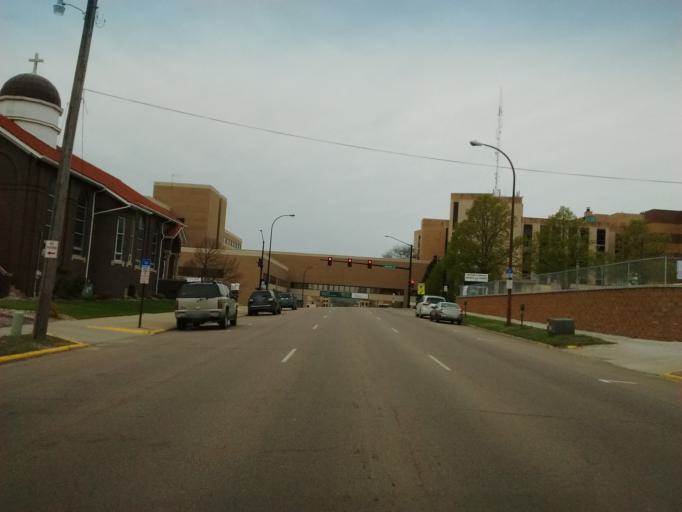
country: US
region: Iowa
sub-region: Woodbury County
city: Sioux City
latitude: 42.4964
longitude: -96.3983
